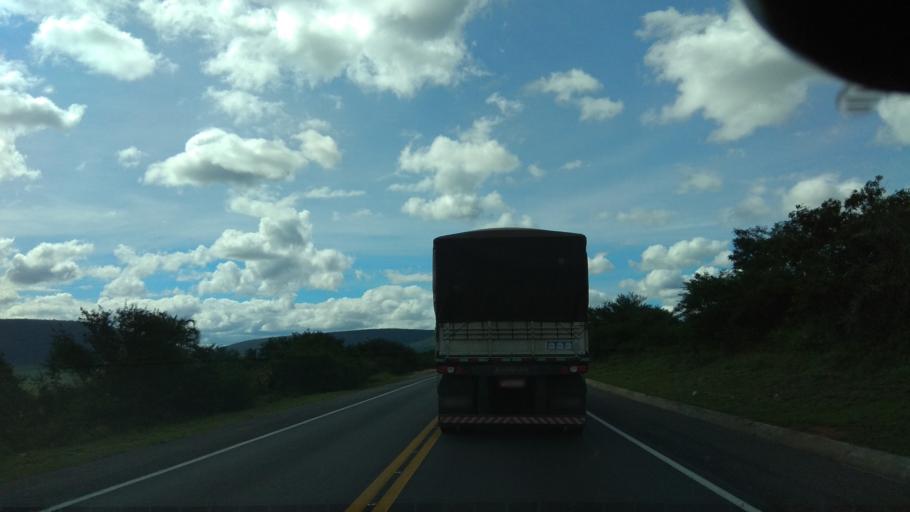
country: BR
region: Bahia
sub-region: Santa Ines
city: Santa Ines
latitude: -13.2872
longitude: -40.0211
